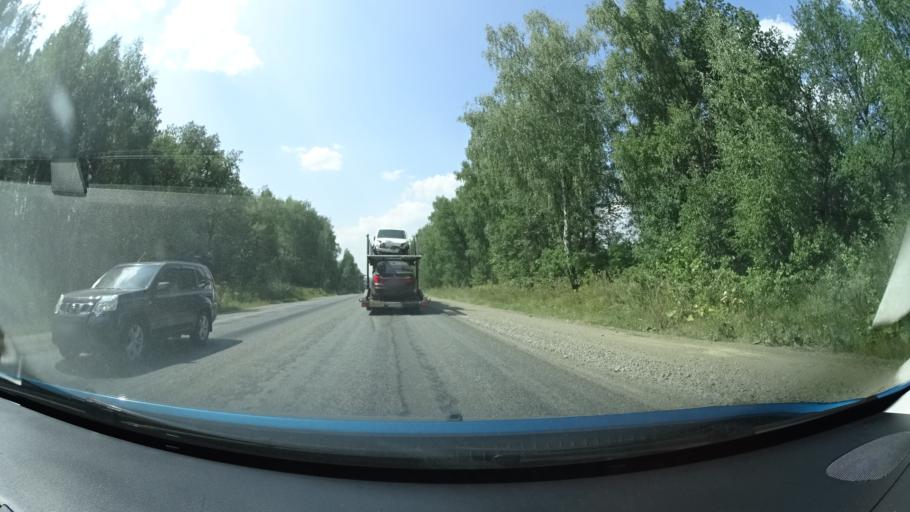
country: RU
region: Bashkortostan
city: Nizhnetroitskiy
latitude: 54.4526
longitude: 53.6431
